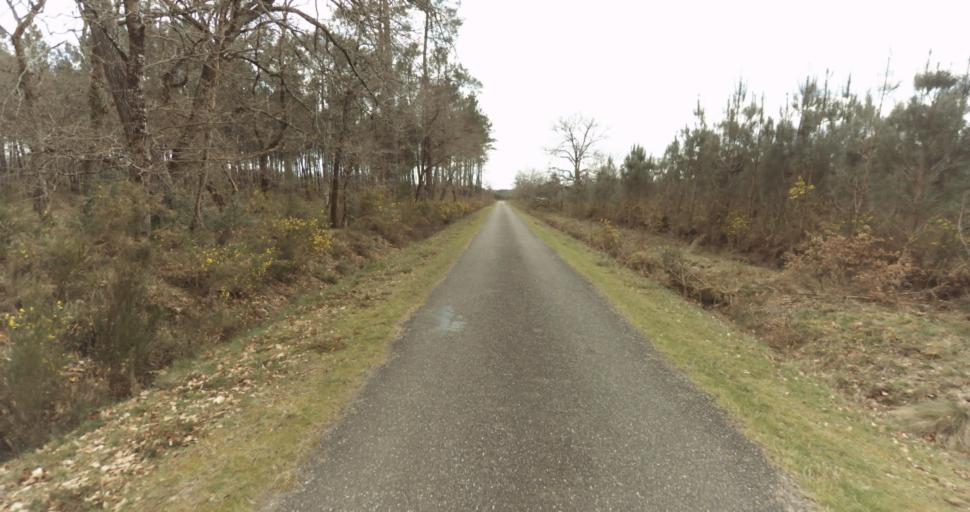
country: FR
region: Aquitaine
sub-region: Departement des Landes
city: Roquefort
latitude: 44.0822
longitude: -0.4411
